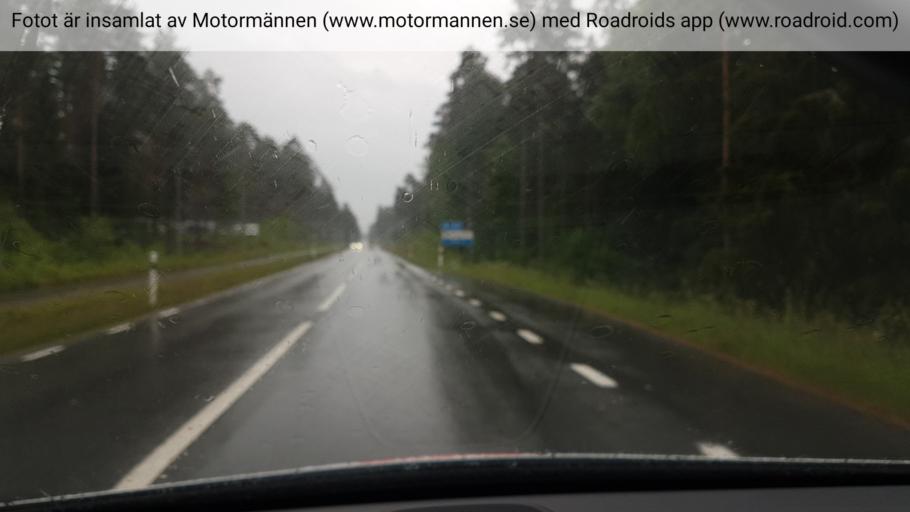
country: SE
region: Joenkoeping
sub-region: Mullsjo Kommun
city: Mullsjoe
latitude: 57.8966
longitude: 13.8409
